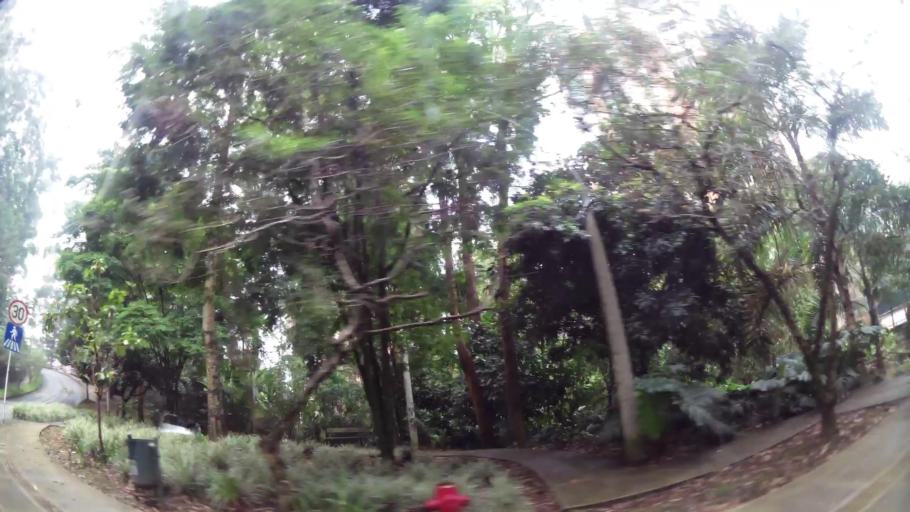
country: CO
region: Antioquia
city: Medellin
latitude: 6.2074
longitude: -75.5564
